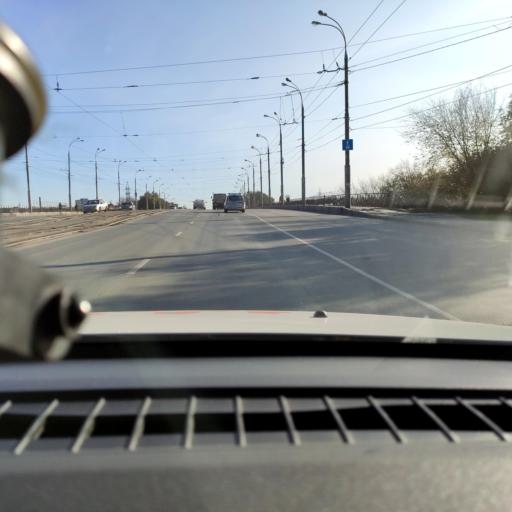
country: RU
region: Samara
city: Samara
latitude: 53.2143
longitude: 50.2690
